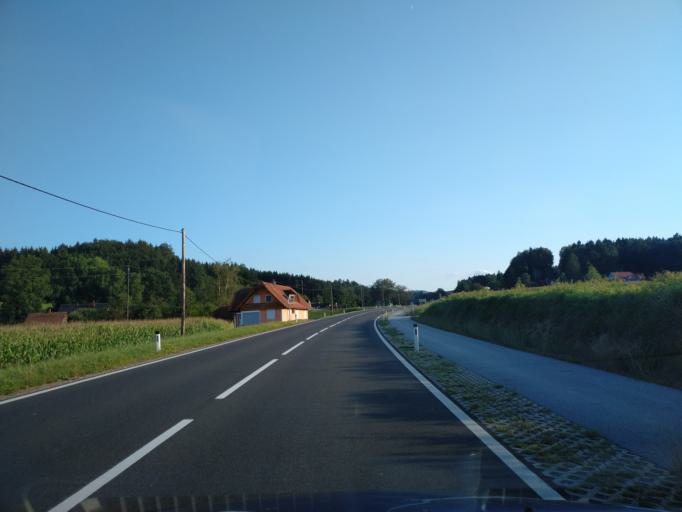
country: AT
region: Styria
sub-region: Politischer Bezirk Deutschlandsberg
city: Pitschgau
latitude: 46.7132
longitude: 15.2526
